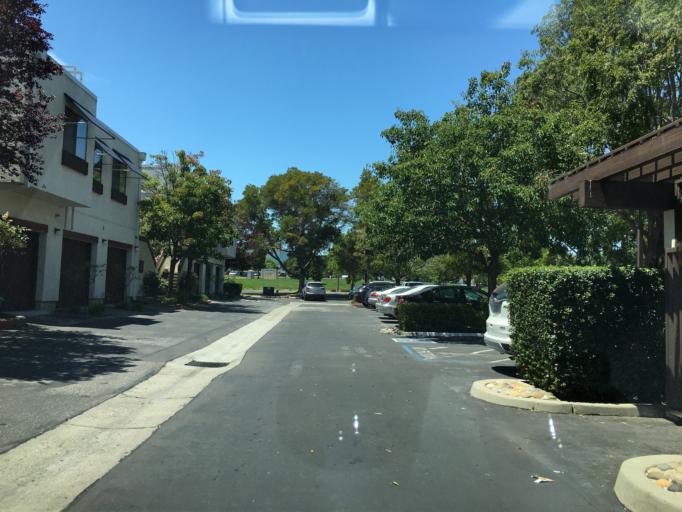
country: US
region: California
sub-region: San Mateo County
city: Redwood Shores
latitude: 37.5335
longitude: -122.2555
